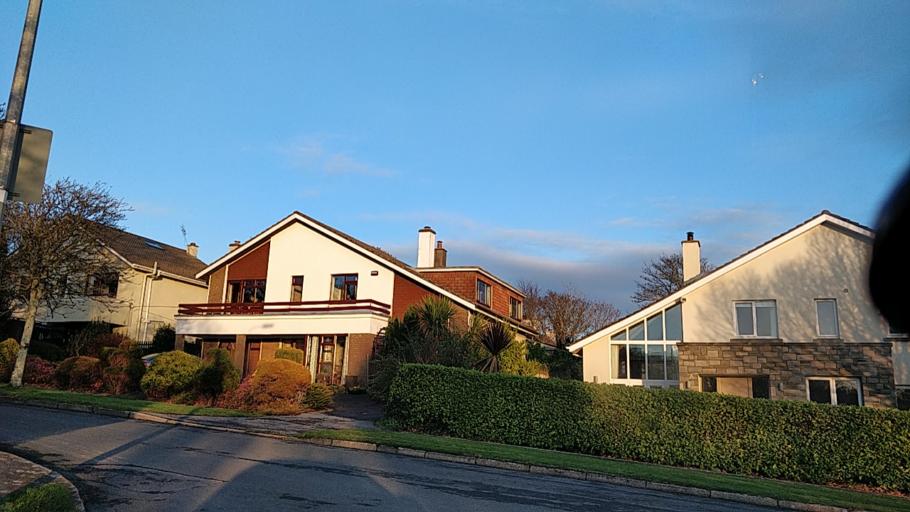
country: IE
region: Connaught
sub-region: County Galway
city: Gaillimh
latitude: 53.2678
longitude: -9.0830
